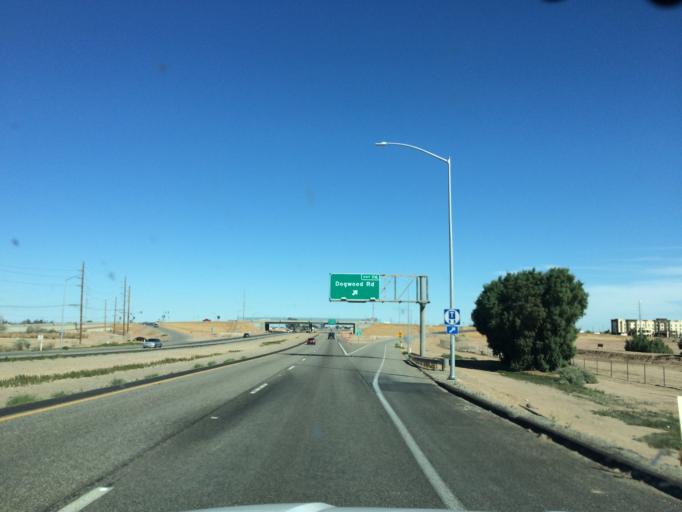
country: US
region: California
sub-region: Imperial County
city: El Centro
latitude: 32.7737
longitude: -115.5396
